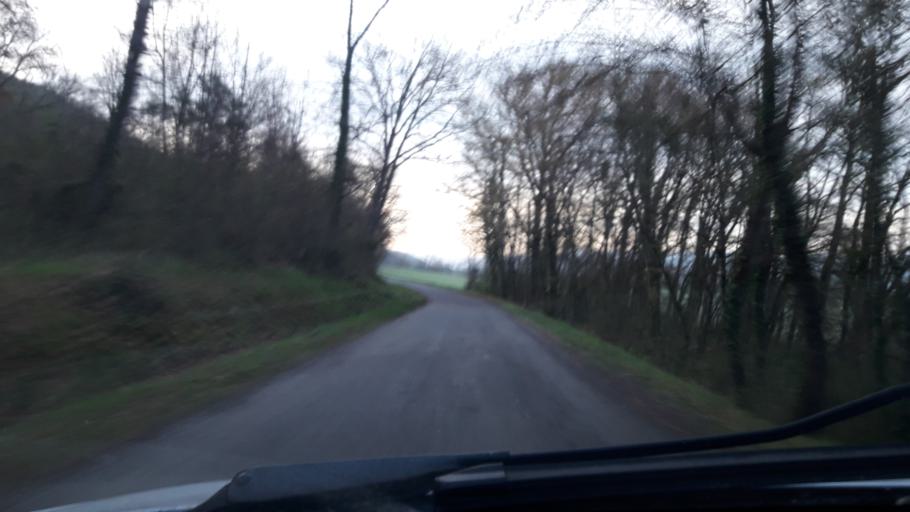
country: FR
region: Midi-Pyrenees
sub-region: Departement de la Haute-Garonne
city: Montesquieu-Volvestre
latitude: 43.1884
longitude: 1.2551
